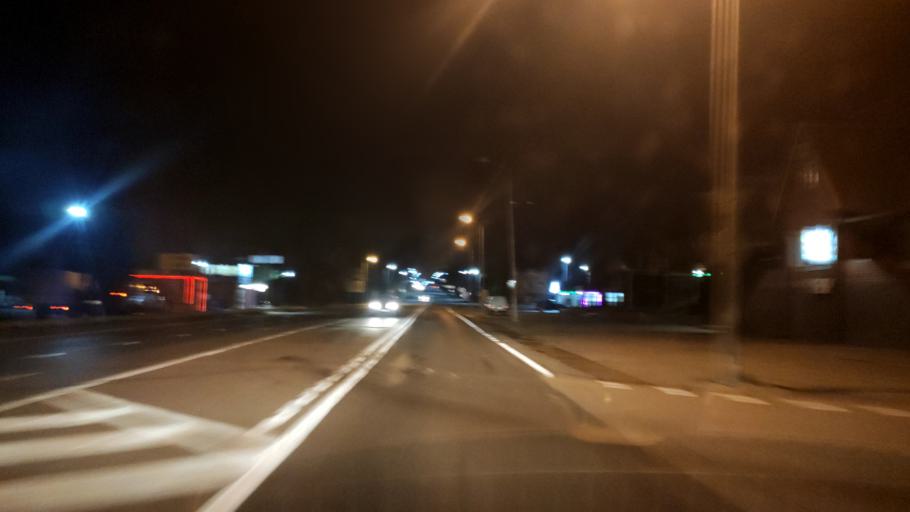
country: RU
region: Belgorod
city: Staryy Oskol
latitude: 51.3545
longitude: 37.8316
